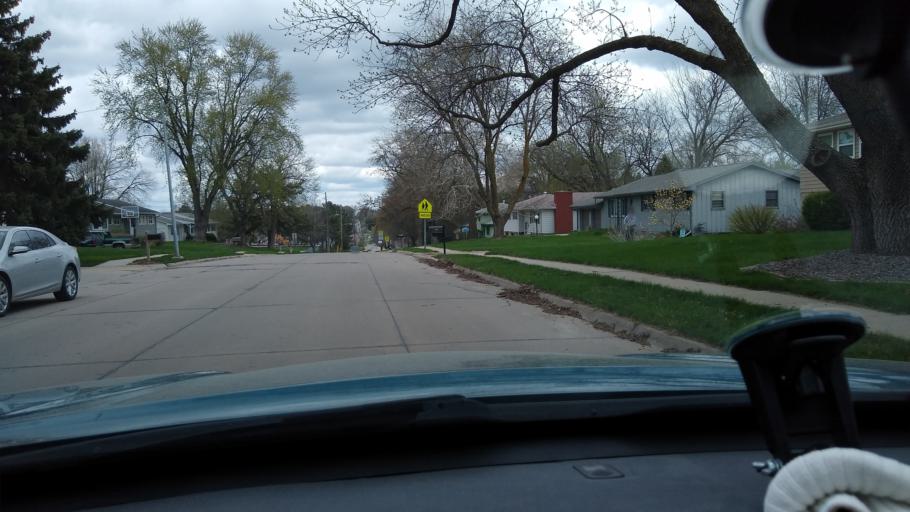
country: US
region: Nebraska
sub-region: Douglas County
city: Ralston
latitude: 41.2279
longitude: -96.0912
